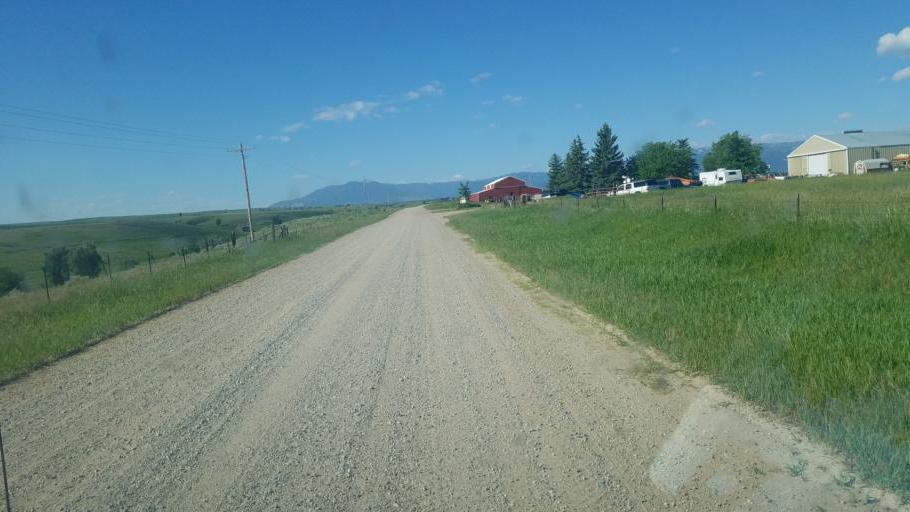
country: US
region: Montana
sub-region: Carbon County
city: Red Lodge
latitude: 45.3375
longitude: -109.1620
